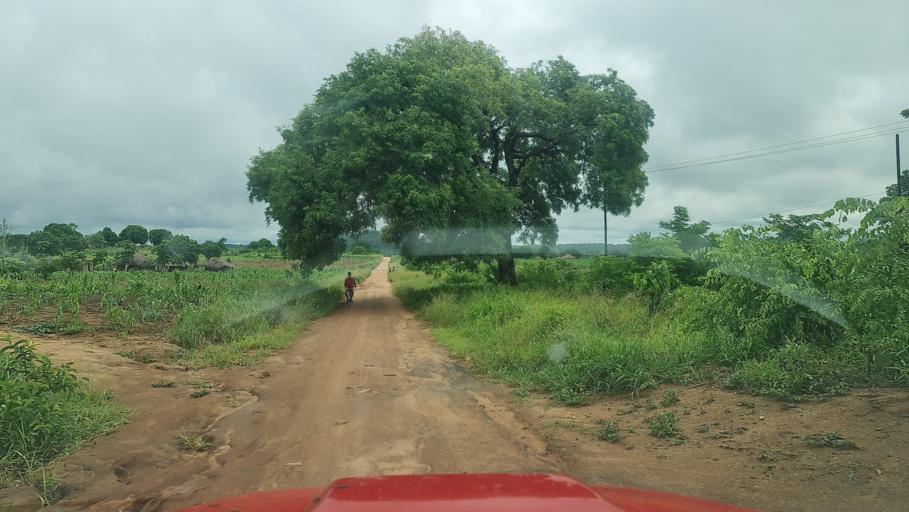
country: MW
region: Southern Region
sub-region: Nsanje District
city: Nsanje
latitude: -17.1849
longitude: 35.9252
